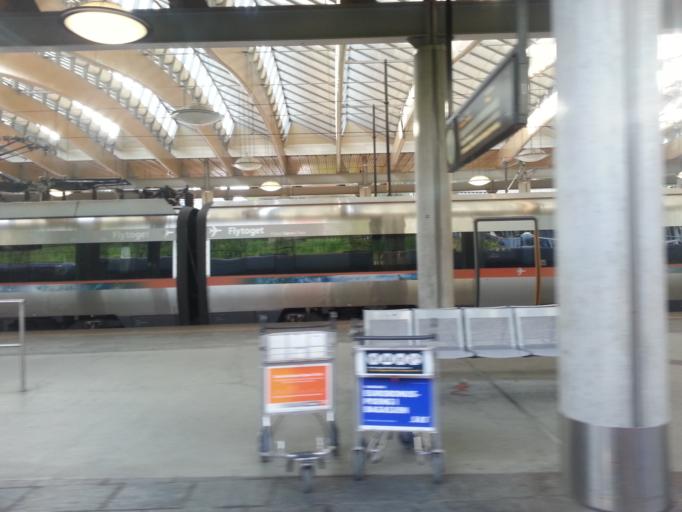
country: NO
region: Akershus
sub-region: Nannestad
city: Teigebyen
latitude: 60.1934
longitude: 11.0968
